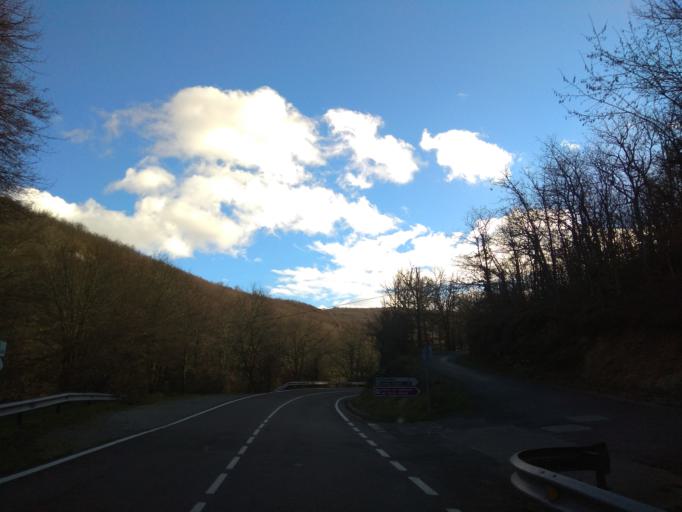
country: ES
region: Cantabria
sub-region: Provincia de Cantabria
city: San Martin de Elines
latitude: 42.8737
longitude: -3.9138
